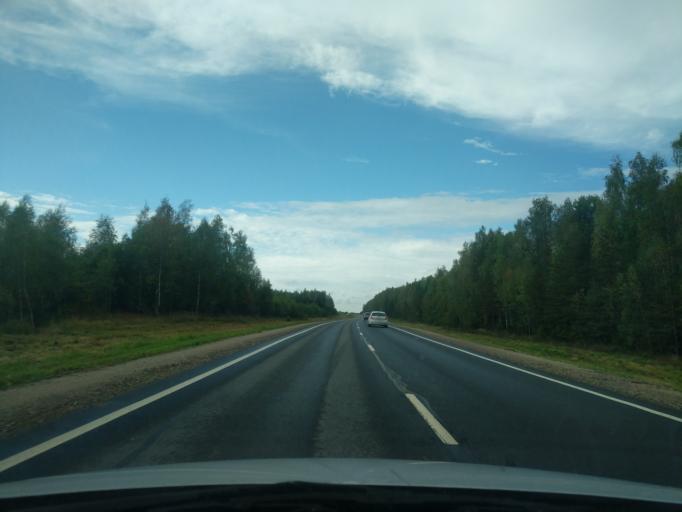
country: RU
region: Kostroma
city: Ostrovskoye
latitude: 57.8143
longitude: 41.9782
